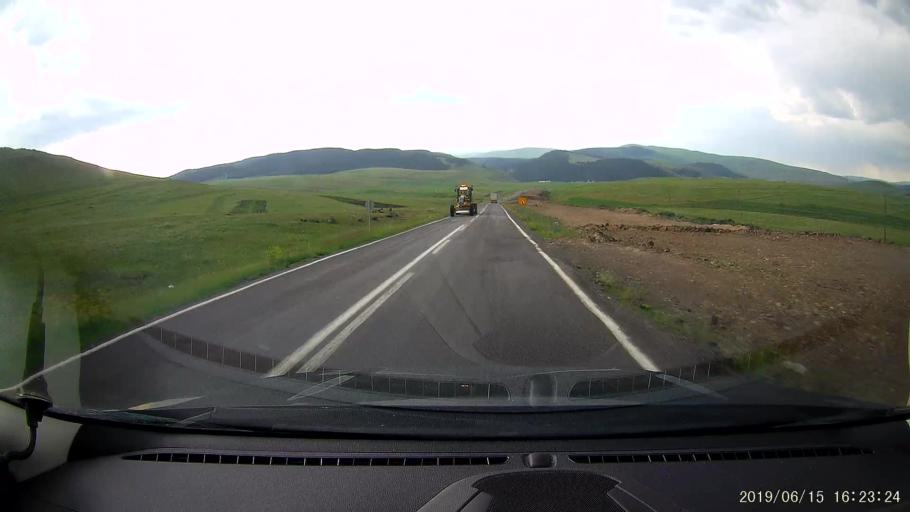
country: TR
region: Ardahan
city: Hanak
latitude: 41.1783
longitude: 42.8621
